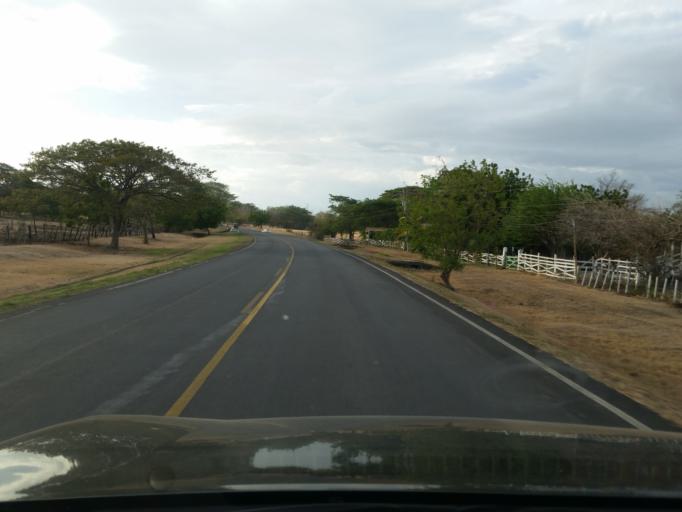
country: NI
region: Rivas
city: Belen
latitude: 11.5798
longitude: -85.8995
